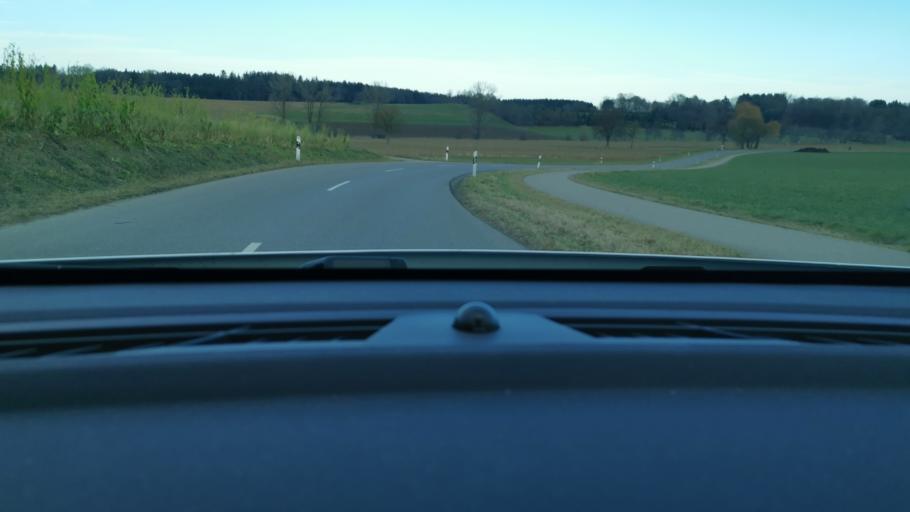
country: DE
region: Bavaria
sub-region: Swabia
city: Affing
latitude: 48.4978
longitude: 10.9890
